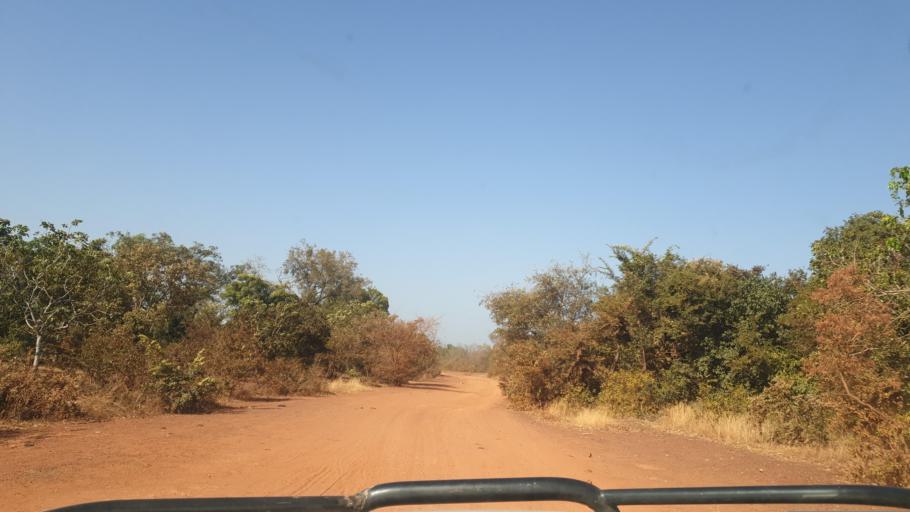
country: ML
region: Sikasso
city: Bougouni
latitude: 11.8207
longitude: -6.9582
